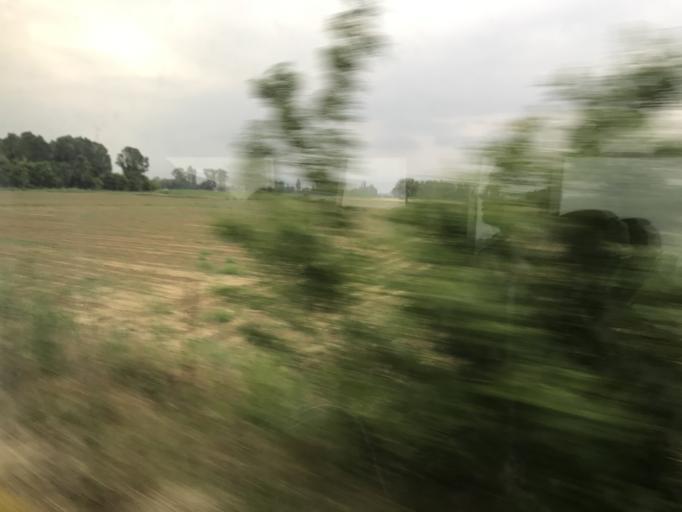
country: GR
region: East Macedonia and Thrace
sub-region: Nomos Rodopis
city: Aratos
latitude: 41.0785
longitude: 25.5698
